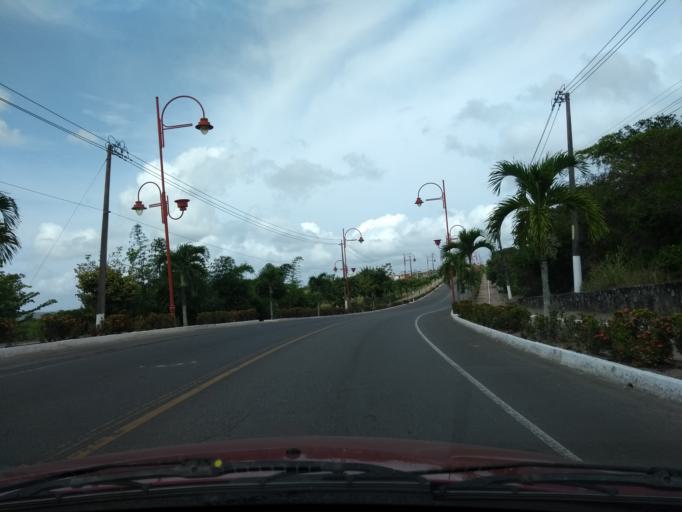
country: BR
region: Bahia
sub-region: Sao Francisco Do Conde
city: Sao Francisco do Conde
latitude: -12.6153
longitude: -38.6577
